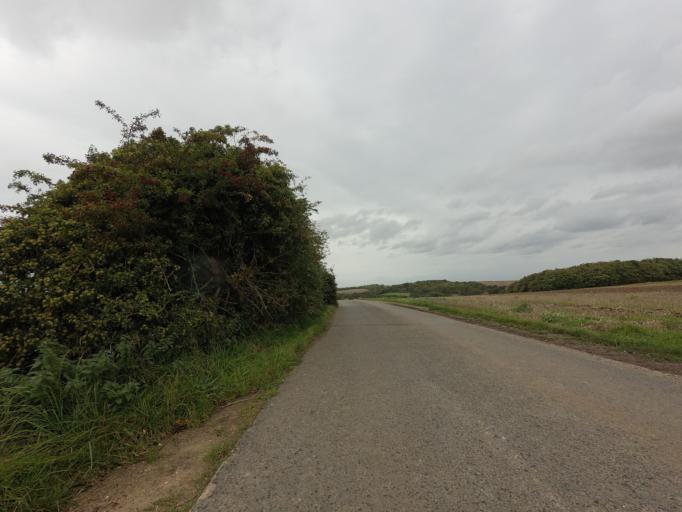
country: GB
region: England
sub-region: Cambridgeshire
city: Duxford
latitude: 52.0501
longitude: 0.1366
